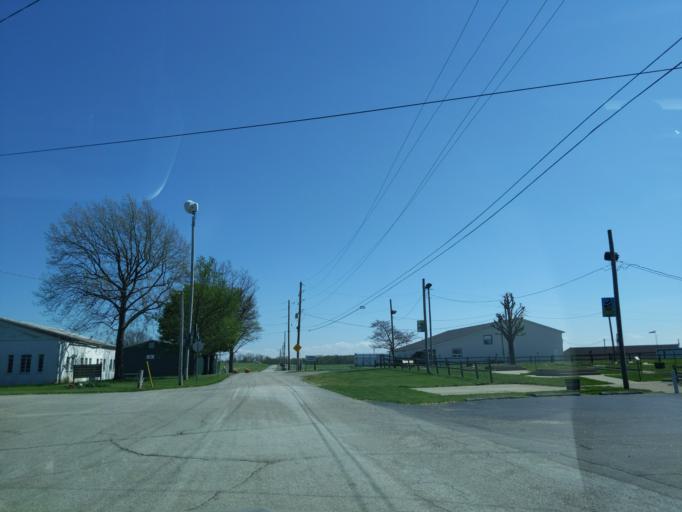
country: US
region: Indiana
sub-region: Decatur County
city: Greensburg
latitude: 39.3290
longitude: -85.5183
